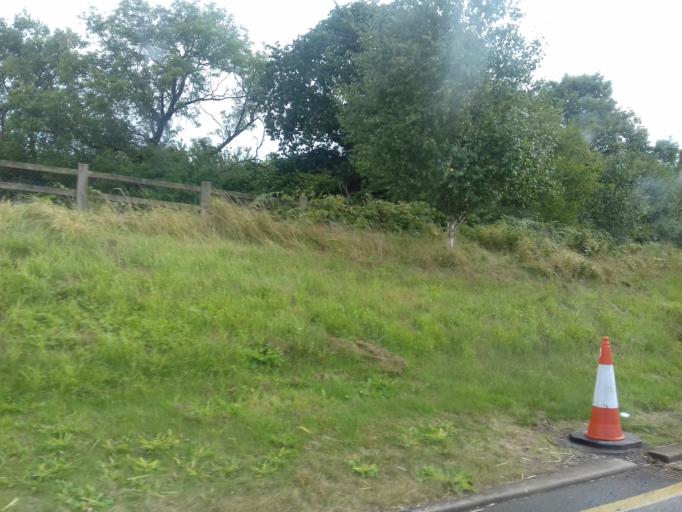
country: IE
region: Munster
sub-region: Waterford
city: Waterford
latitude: 52.2738
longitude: -7.1581
